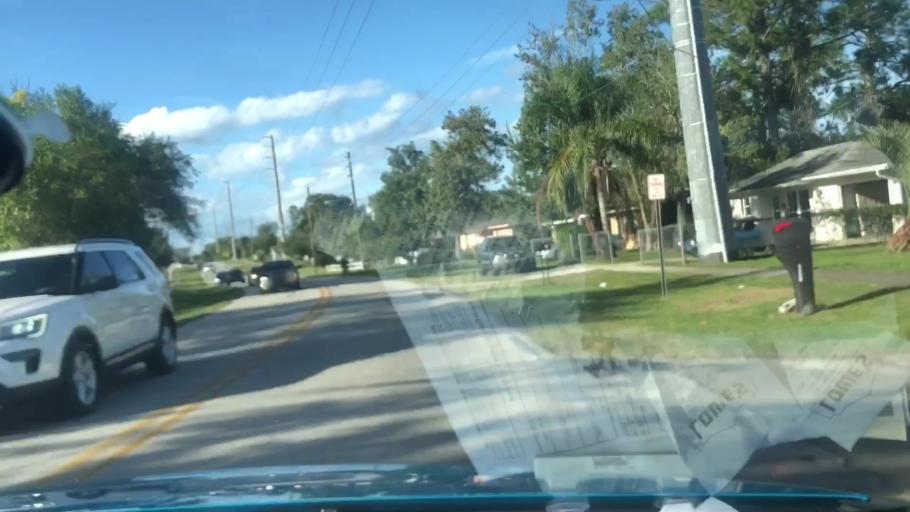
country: US
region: Florida
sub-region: Volusia County
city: Deltona
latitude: 28.8952
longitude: -81.2332
